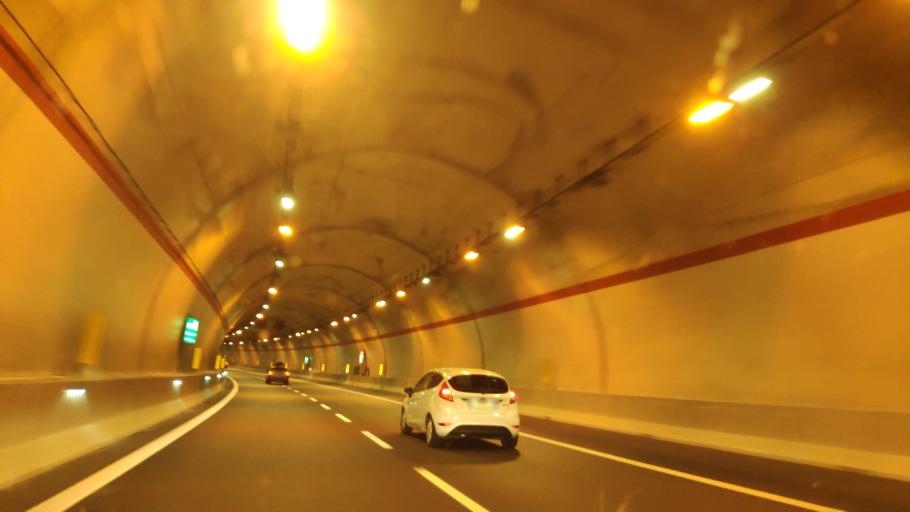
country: IT
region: Calabria
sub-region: Provincia di Cosenza
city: Laino Borgo
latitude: 39.9453
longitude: 15.9590
